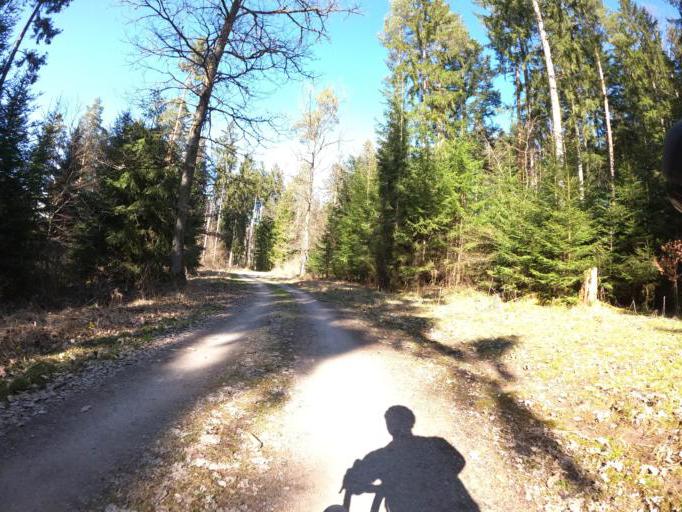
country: DE
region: Baden-Wuerttemberg
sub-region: Tuebingen Region
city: Hirrlingen
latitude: 48.4056
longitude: 8.9326
